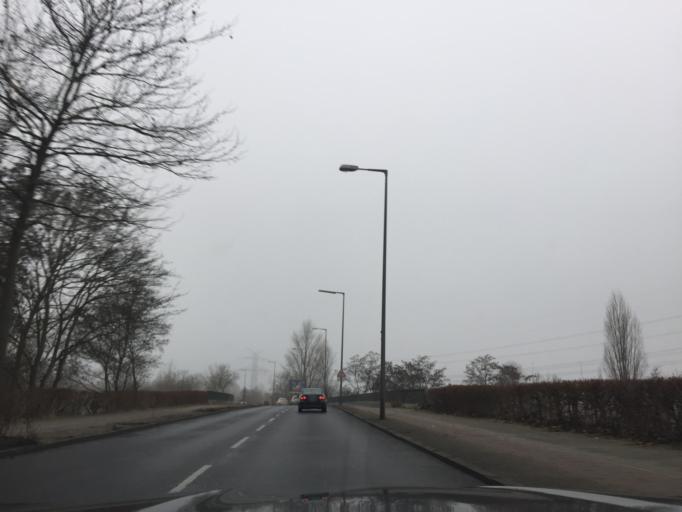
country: DE
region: Berlin
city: Westend
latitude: 52.5276
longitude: 13.2752
